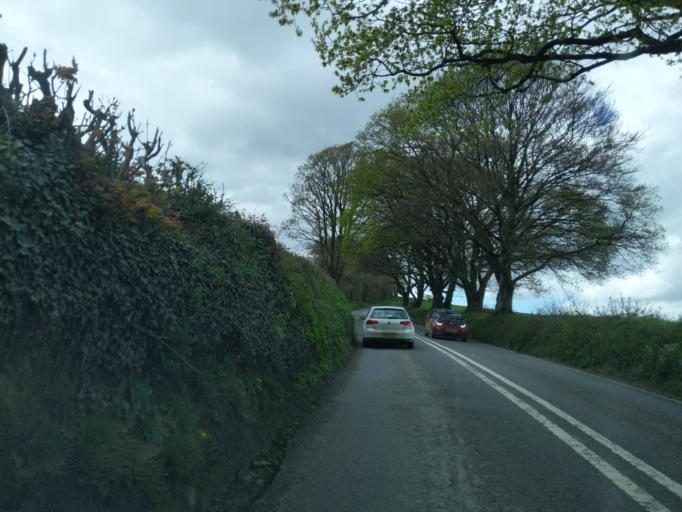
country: GB
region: England
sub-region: Cornwall
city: Callington
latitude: 50.4864
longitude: -4.3509
